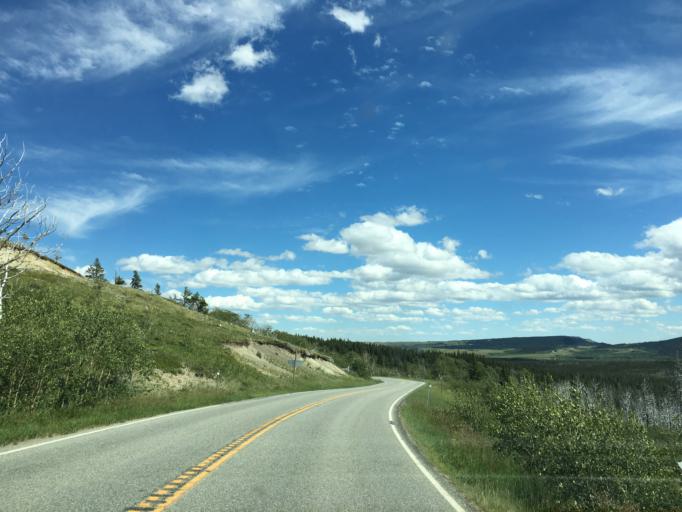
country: US
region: Montana
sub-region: Glacier County
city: North Browning
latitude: 48.6799
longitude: -113.3558
